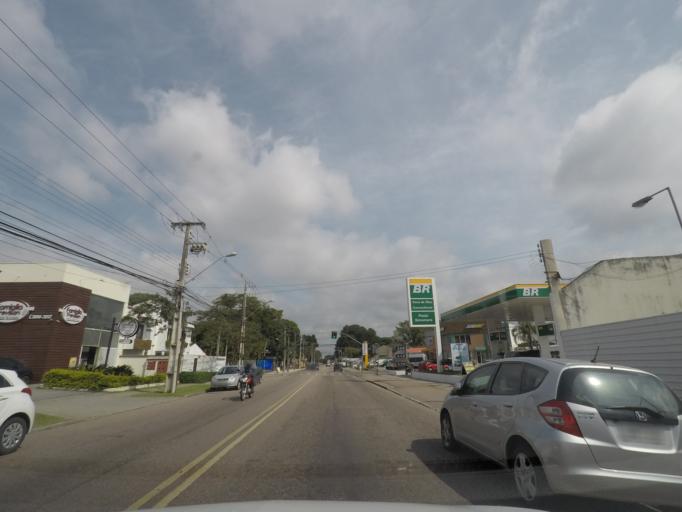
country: BR
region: Parana
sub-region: Curitiba
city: Curitiba
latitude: -25.4754
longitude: -49.3027
